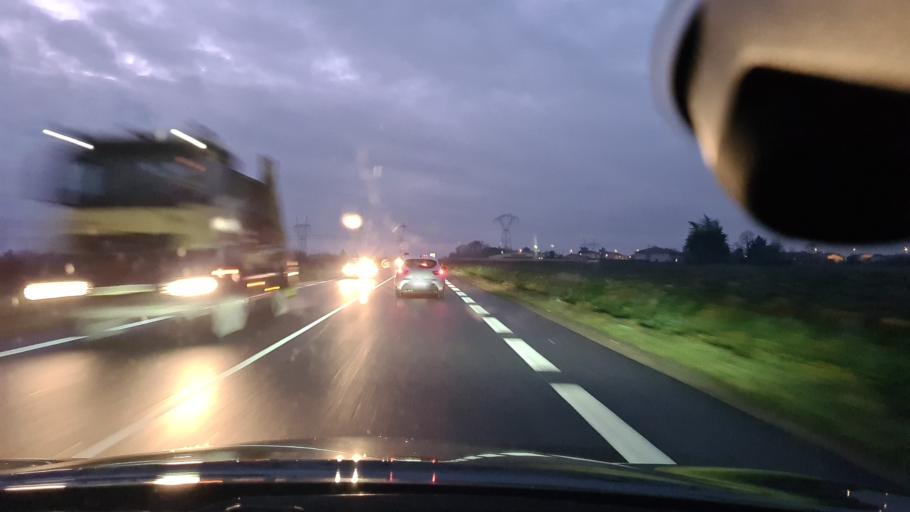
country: FR
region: Rhone-Alpes
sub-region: Departement du Rhone
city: Genas
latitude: 45.7322
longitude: 5.0277
